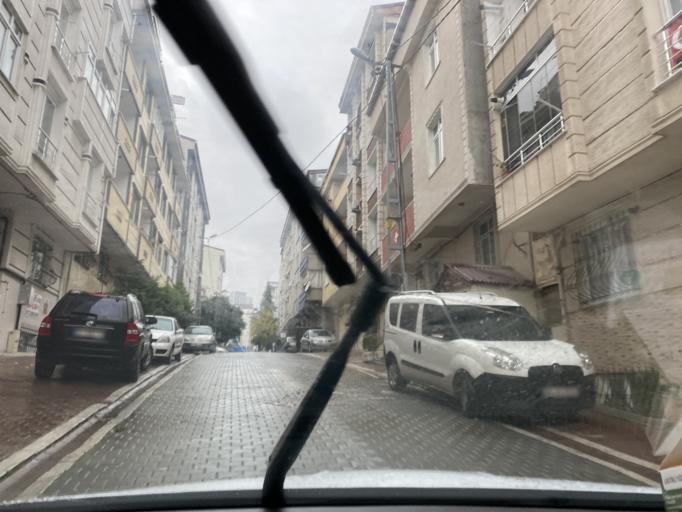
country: TR
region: Istanbul
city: Esenyurt
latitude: 41.0201
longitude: 28.6665
